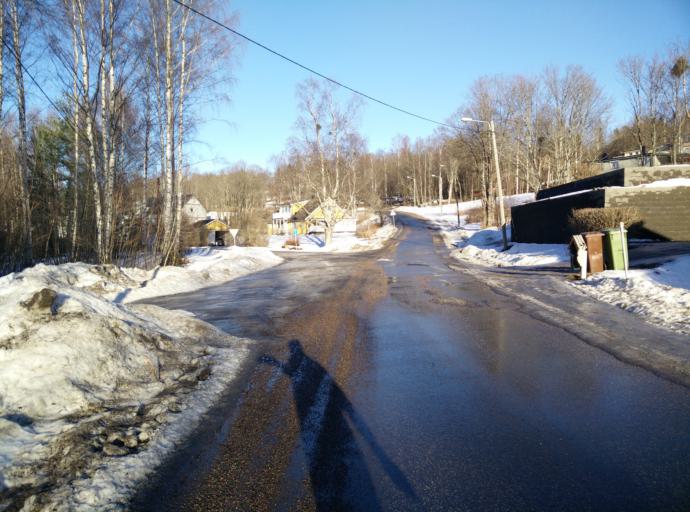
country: SE
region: Vaesternorrland
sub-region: Sundsvalls Kommun
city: Skottsund
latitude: 62.3109
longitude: 17.3920
